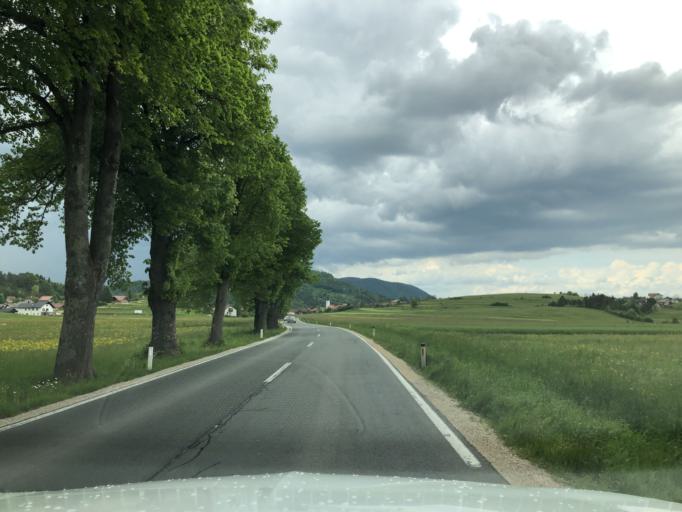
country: SI
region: Cerknica
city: Rakek
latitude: 45.8158
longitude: 14.3022
